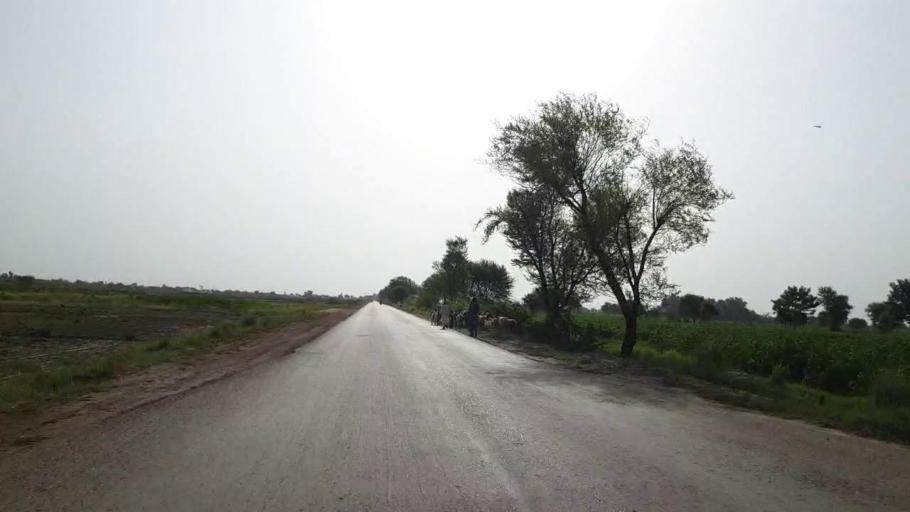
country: PK
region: Sindh
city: Nawabshah
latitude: 26.2580
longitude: 68.4754
